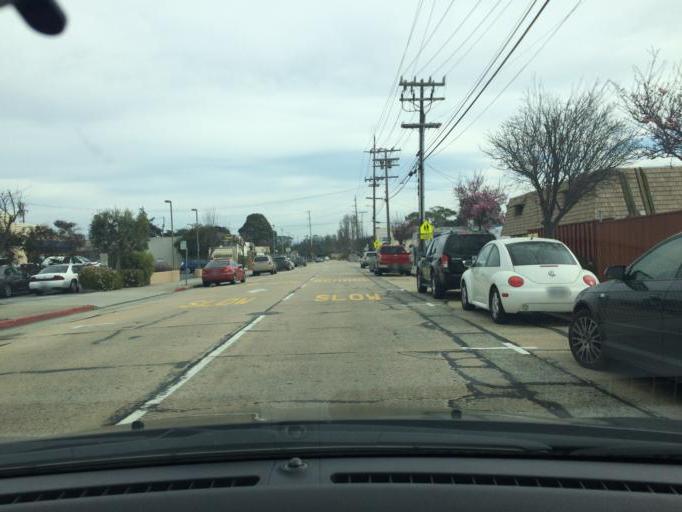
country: US
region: California
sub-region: Monterey County
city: Monterey
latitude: 36.5993
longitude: -121.8902
